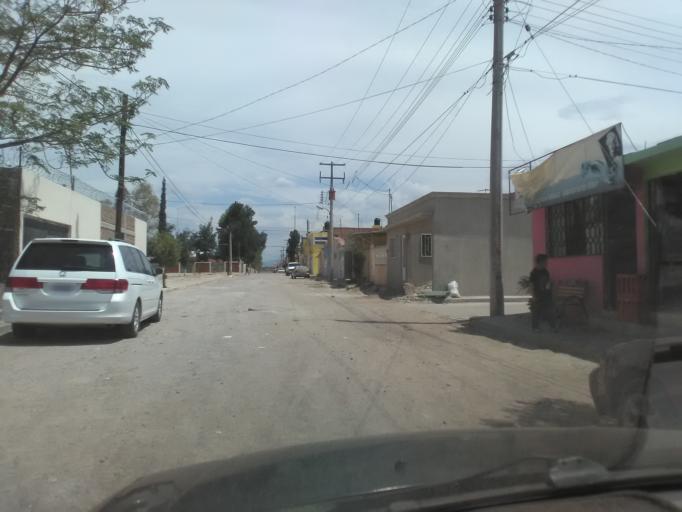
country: MX
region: Durango
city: Victoria de Durango
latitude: 24.0096
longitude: -104.6286
